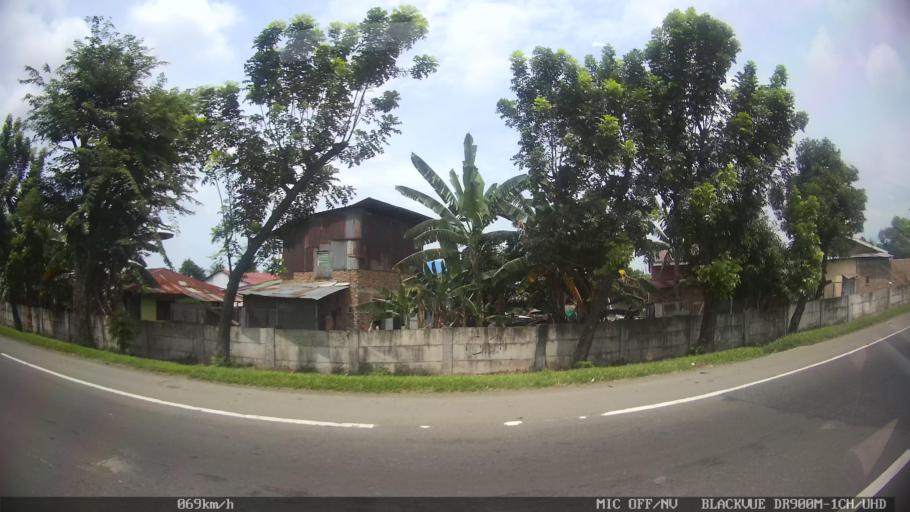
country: ID
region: North Sumatra
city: Labuhan Deli
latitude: 3.6632
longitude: 98.6822
